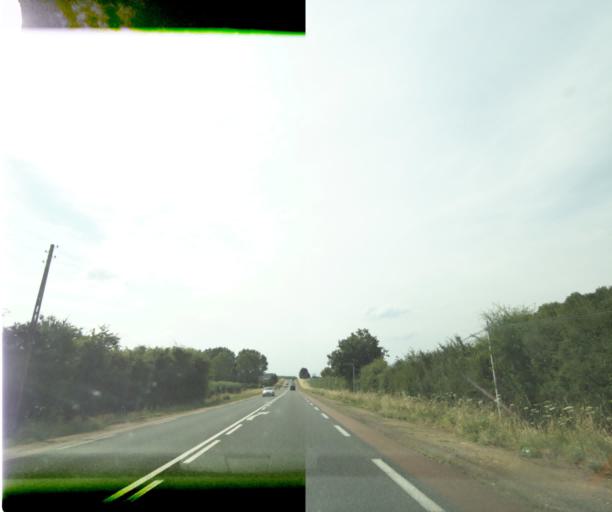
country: FR
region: Pays de la Loire
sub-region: Departement de la Sarthe
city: Luceau
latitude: 47.7413
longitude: 0.3871
